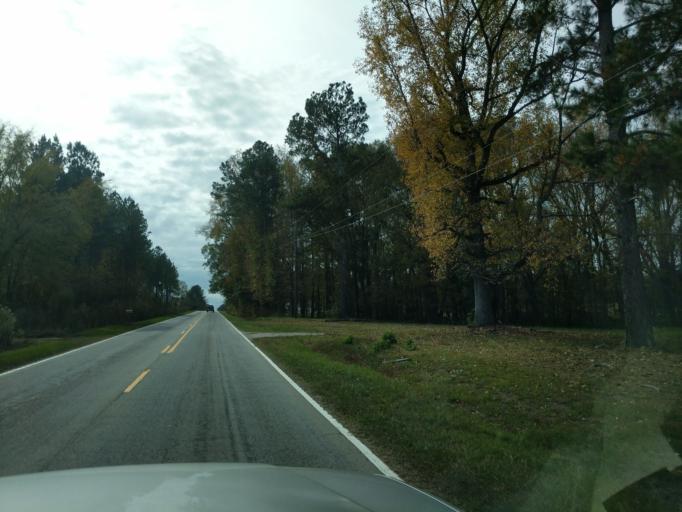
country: US
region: South Carolina
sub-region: Greenwood County
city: Ninety Six
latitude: 34.2161
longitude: -81.8810
